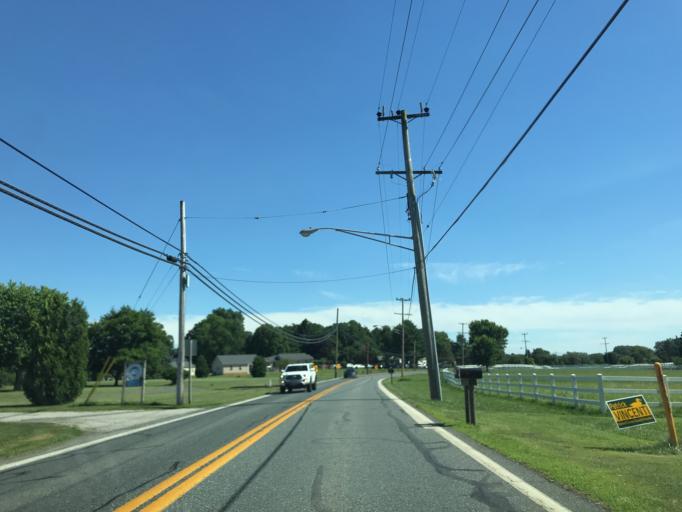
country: US
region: Maryland
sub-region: Harford County
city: Riverside
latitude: 39.5477
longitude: -76.2526
